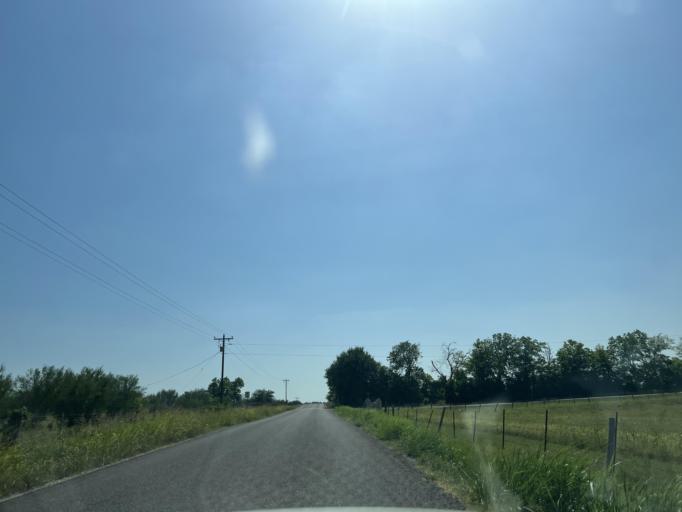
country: US
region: Texas
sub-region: Washington County
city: Brenham
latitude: 30.1585
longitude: -96.3436
